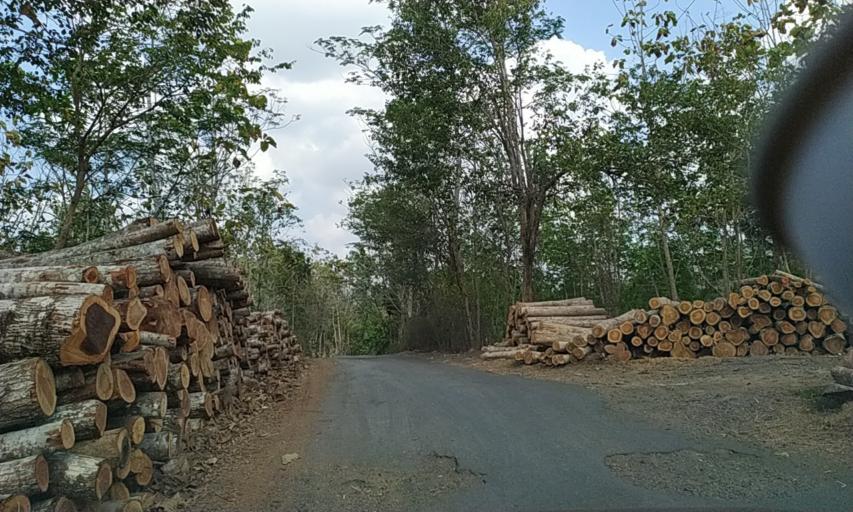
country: ID
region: Central Java
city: Jambuandap
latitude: -7.5713
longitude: 109.0168
